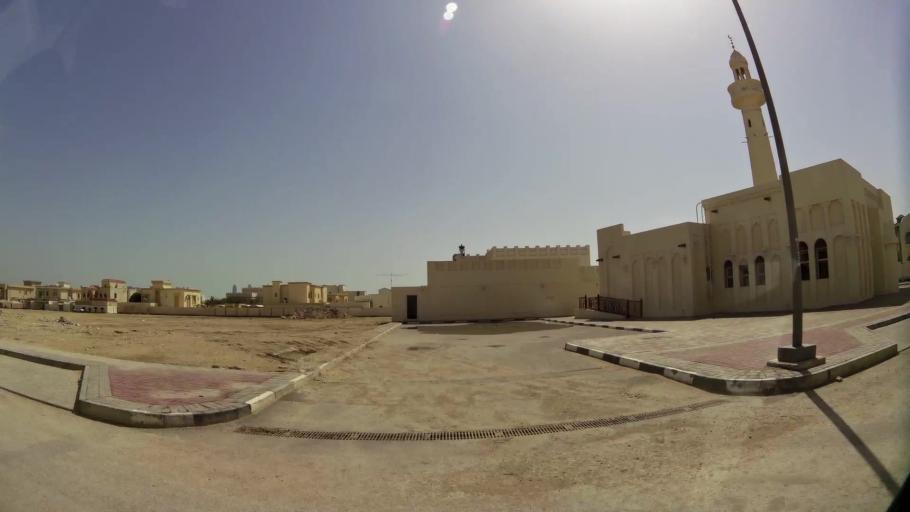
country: QA
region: Baladiyat ad Dawhah
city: Doha
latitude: 25.3572
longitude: 51.4969
